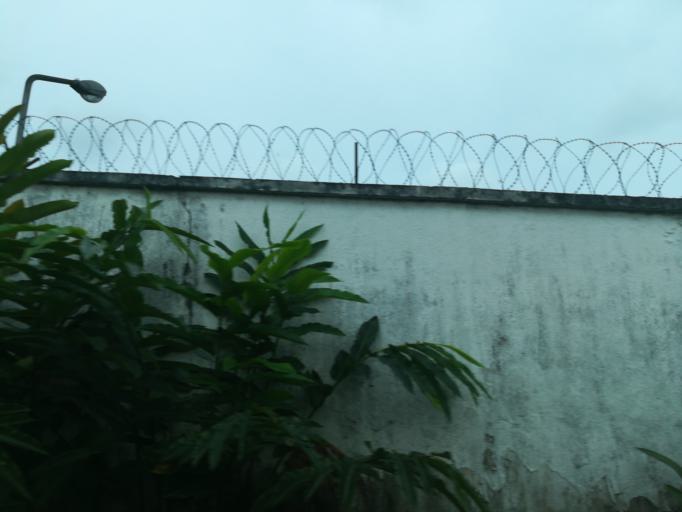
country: NG
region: Rivers
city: Port Harcourt
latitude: 4.8164
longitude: 6.9941
